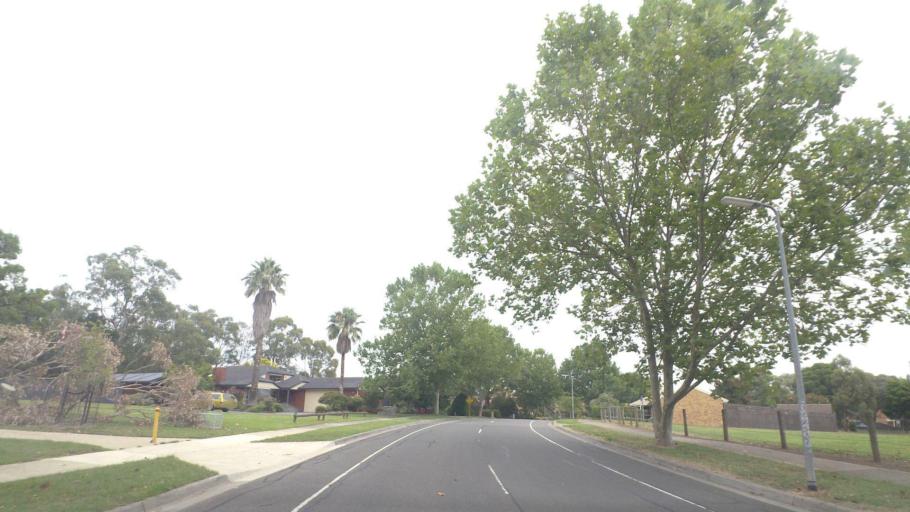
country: AU
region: Victoria
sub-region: Yarra Ranges
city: Lilydale
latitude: -37.7781
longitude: 145.3383
